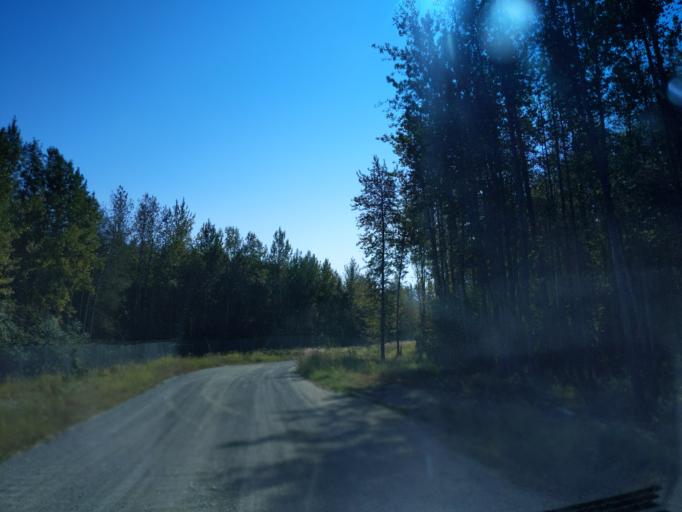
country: US
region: Alaska
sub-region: Anchorage Municipality
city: Anchorage
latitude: 61.1607
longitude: -150.0125
